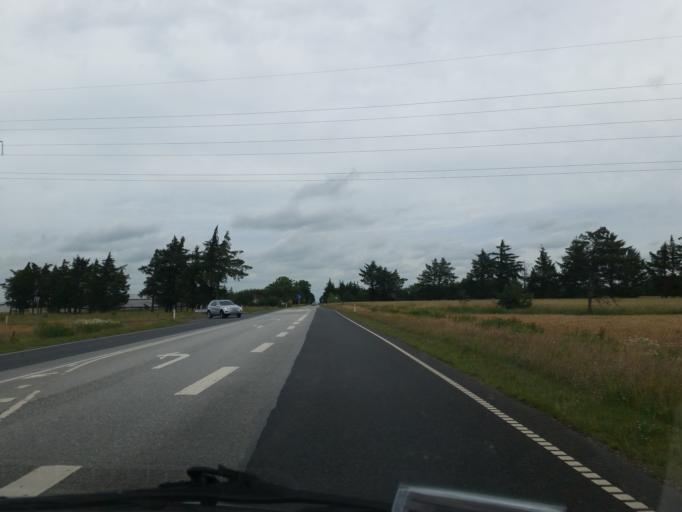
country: DK
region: South Denmark
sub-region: Esbjerg Kommune
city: Ribe
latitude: 55.3562
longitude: 8.7898
